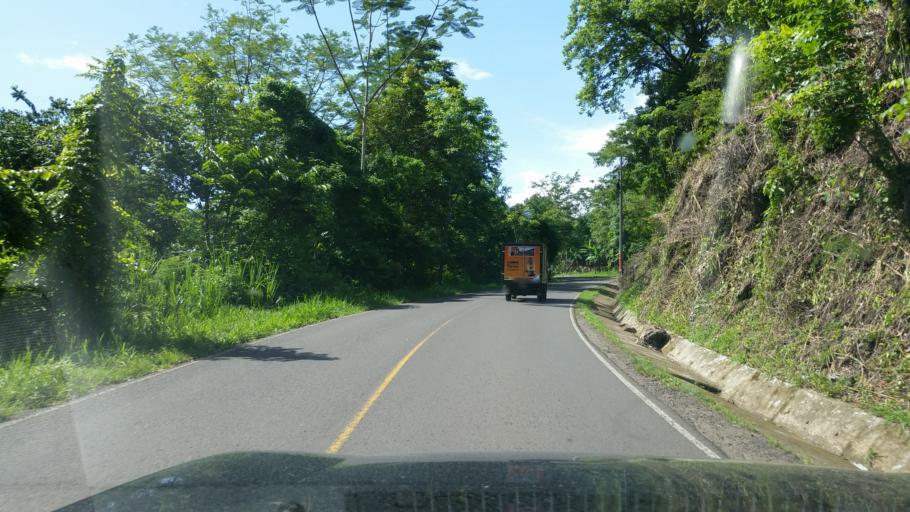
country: NI
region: Matagalpa
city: San Ramon
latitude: 13.0036
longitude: -85.8120
